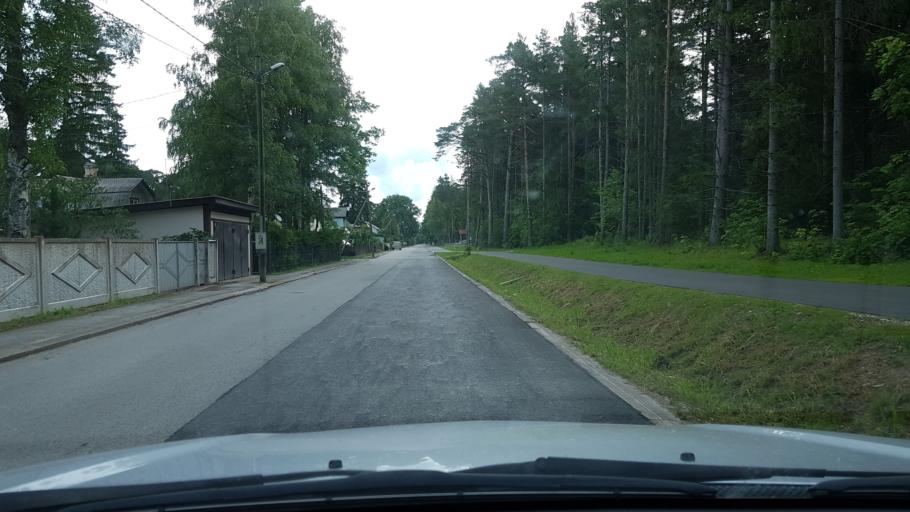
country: EE
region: Ida-Virumaa
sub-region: Narva-Joesuu linn
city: Narva-Joesuu
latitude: 59.4506
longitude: 28.0311
